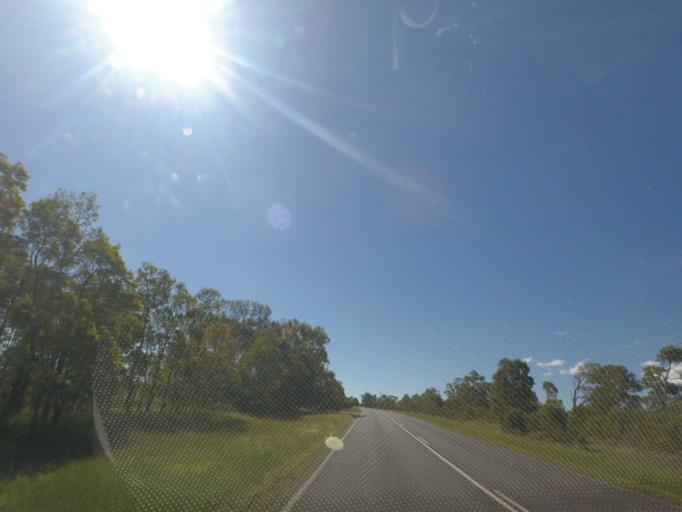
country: AU
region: Victoria
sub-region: Moorabool
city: Bacchus Marsh
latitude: -37.6303
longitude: 144.2149
